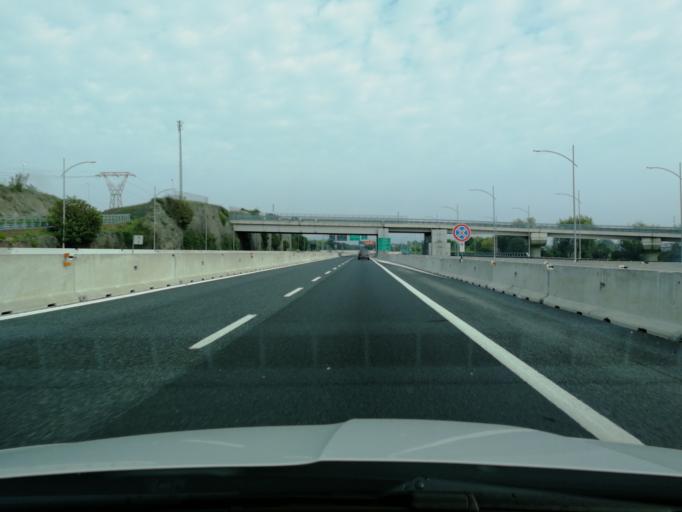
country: IT
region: Latium
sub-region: Citta metropolitana di Roma Capitale
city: Setteville
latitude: 41.9233
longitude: 12.6389
